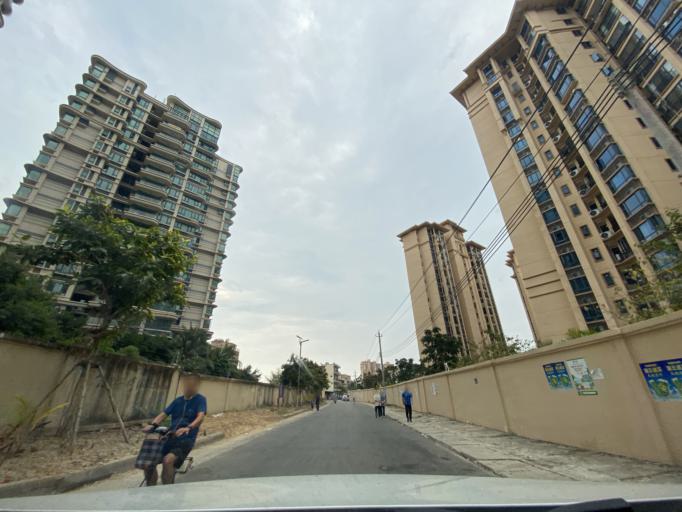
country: CN
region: Hainan
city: Yingzhou
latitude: 18.3973
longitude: 109.8435
